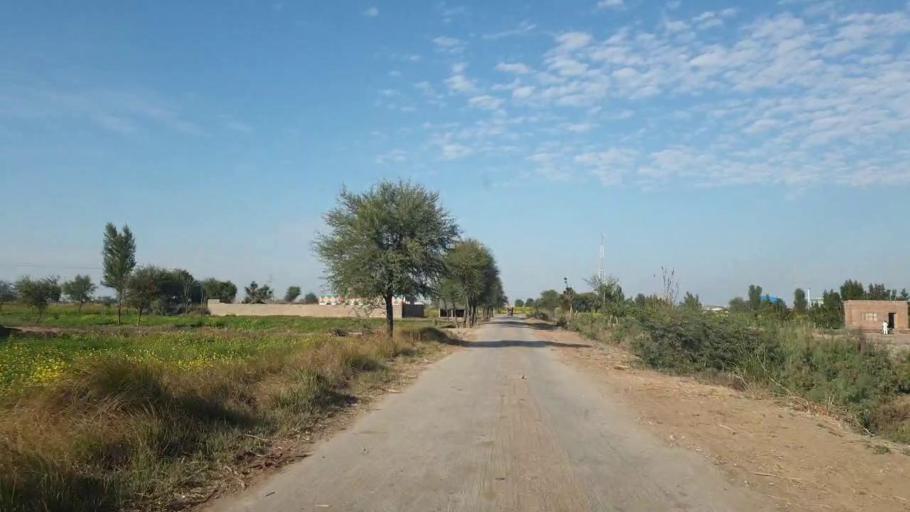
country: PK
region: Sindh
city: Sanghar
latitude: 26.0838
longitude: 68.8764
